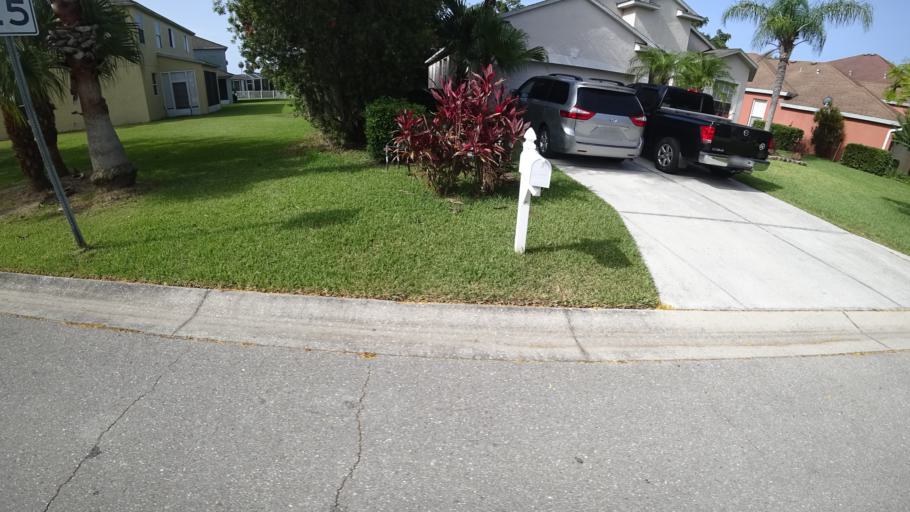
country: US
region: Florida
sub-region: Manatee County
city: Ellenton
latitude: 27.5508
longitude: -82.5044
